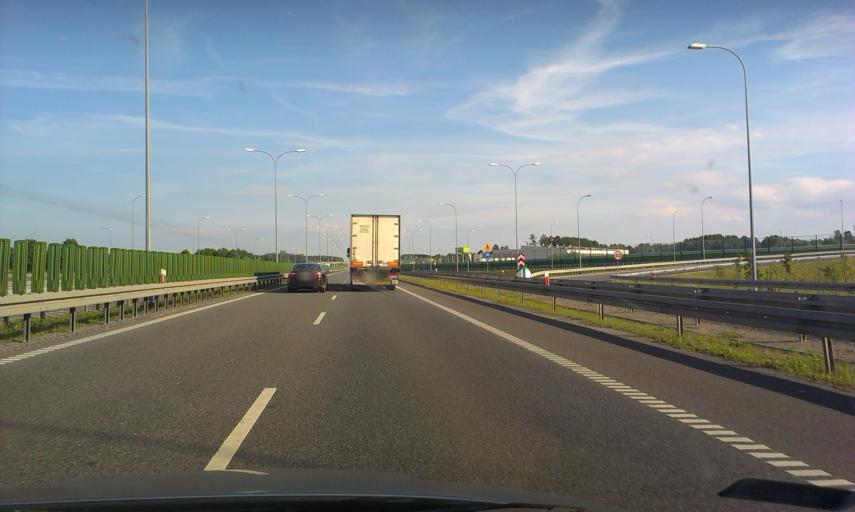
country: PL
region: Kujawsko-Pomorskie
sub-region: Powiat bydgoski
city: Biale Blota
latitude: 53.0947
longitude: 17.8966
